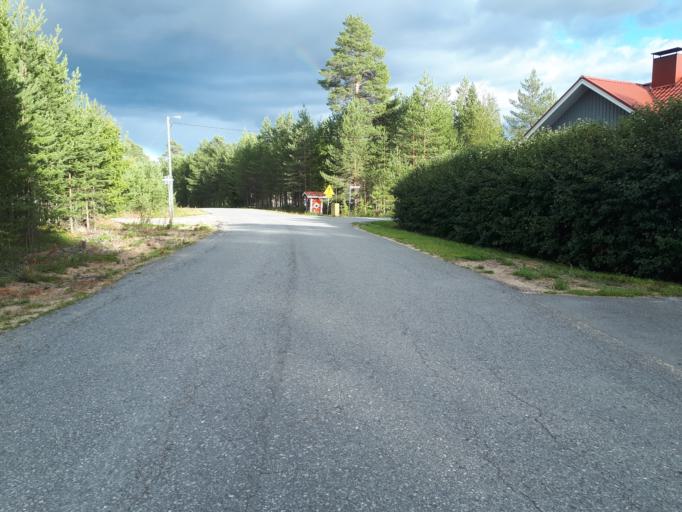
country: FI
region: Northern Ostrobothnia
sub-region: Oulunkaari
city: Ii
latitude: 65.3243
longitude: 25.3982
